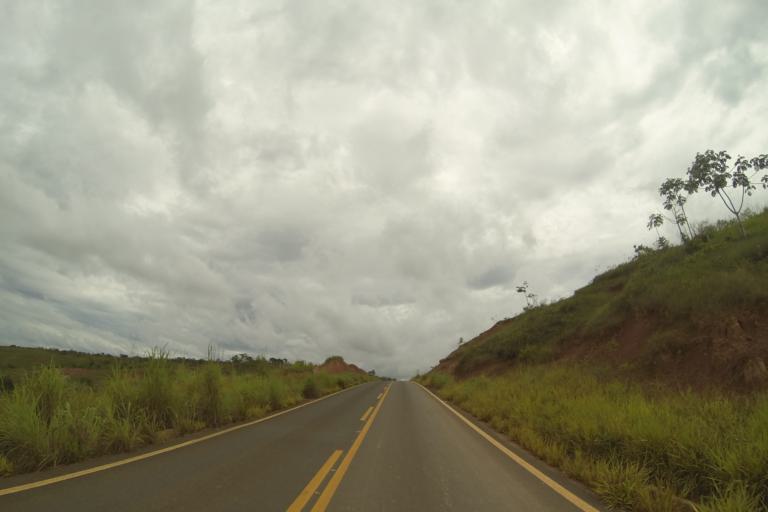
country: BR
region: Minas Gerais
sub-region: Bambui
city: Bambui
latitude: -20.0876
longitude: -46.1342
